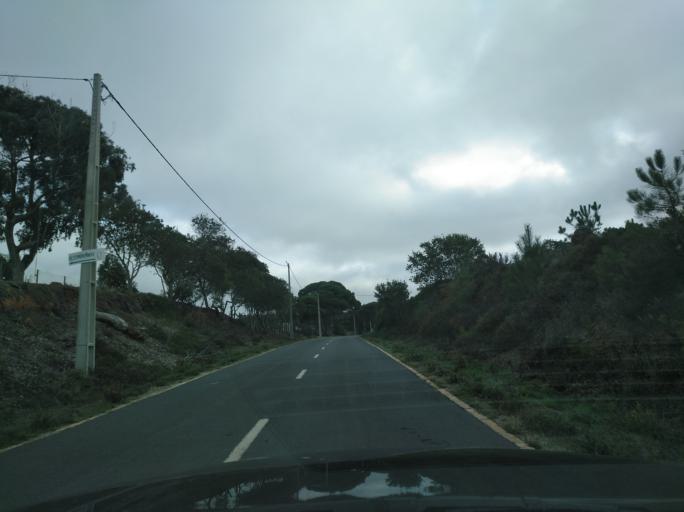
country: PT
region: Beja
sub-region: Odemira
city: Vila Nova de Milfontes
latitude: 37.7066
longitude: -8.7737
